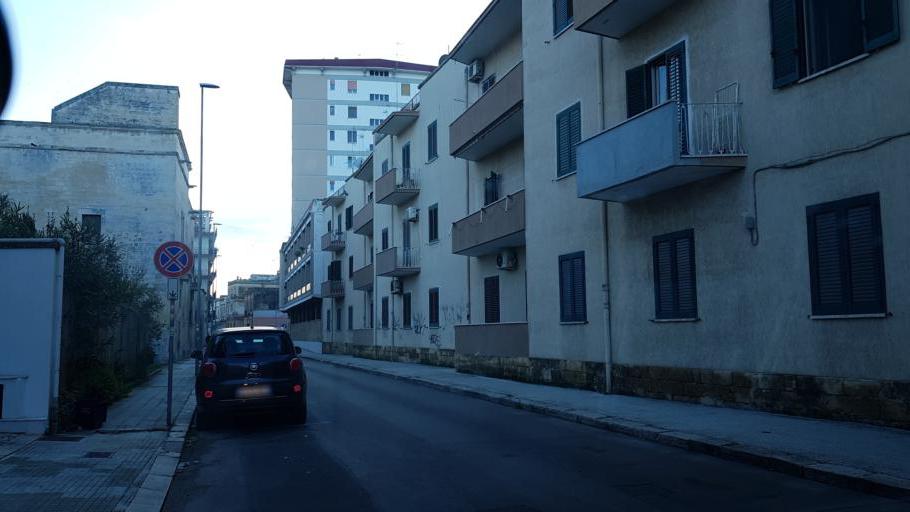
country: IT
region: Apulia
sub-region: Provincia di Lecce
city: Lecce
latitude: 40.3611
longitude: 18.1761
